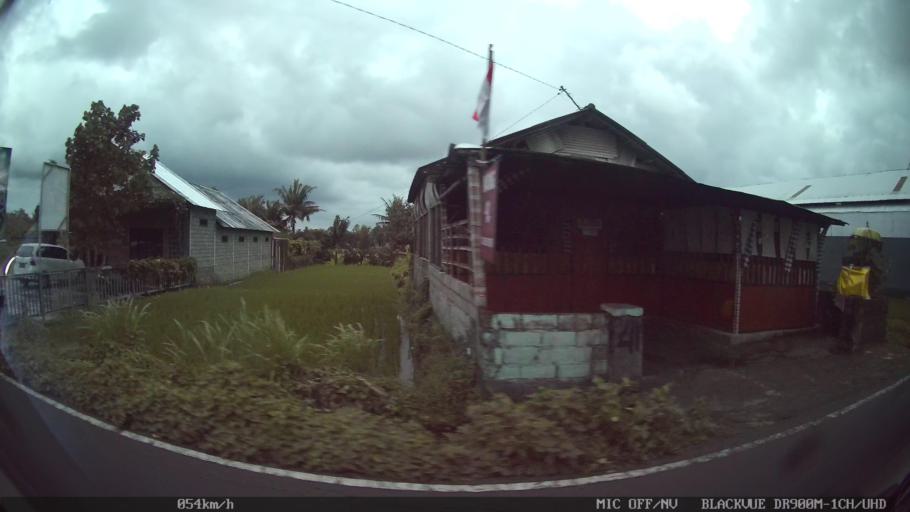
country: ID
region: Bali
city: Banjar Serangan
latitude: -8.5569
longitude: 115.1800
